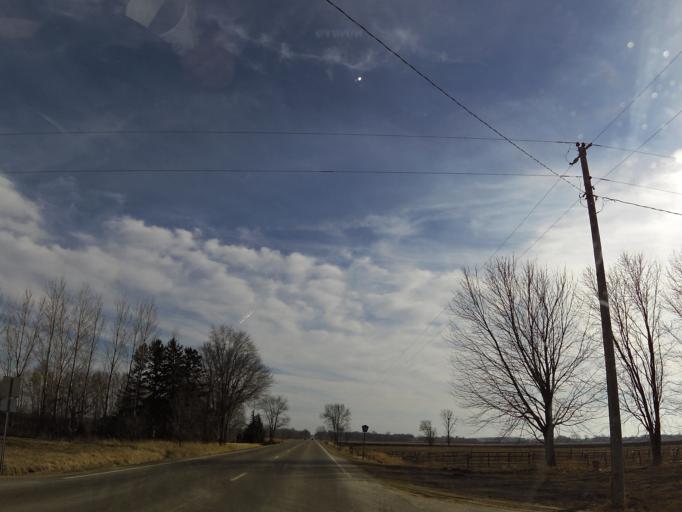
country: US
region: Minnesota
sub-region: Rice County
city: Northfield
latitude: 44.5043
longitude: -93.2003
